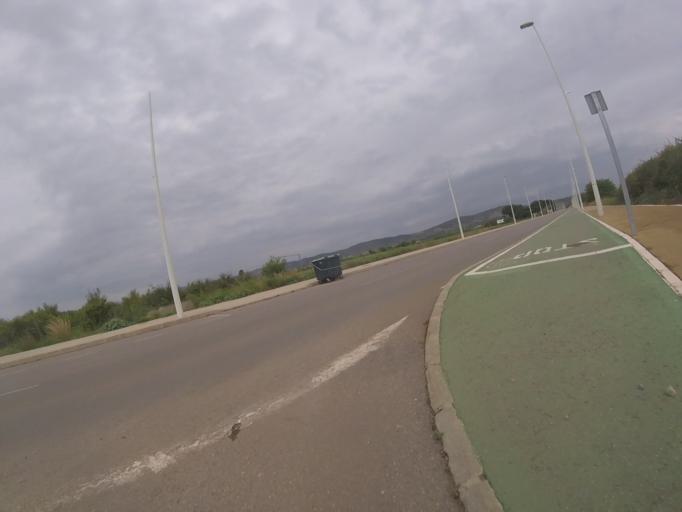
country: ES
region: Valencia
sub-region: Provincia de Castello
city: Torreblanca
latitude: 40.2193
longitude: 0.2175
